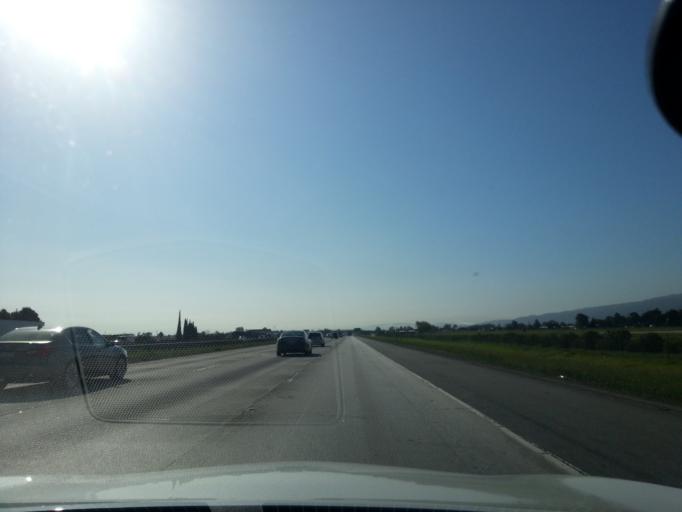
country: US
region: California
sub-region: Santa Clara County
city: San Martin
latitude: 37.0799
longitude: -121.5947
